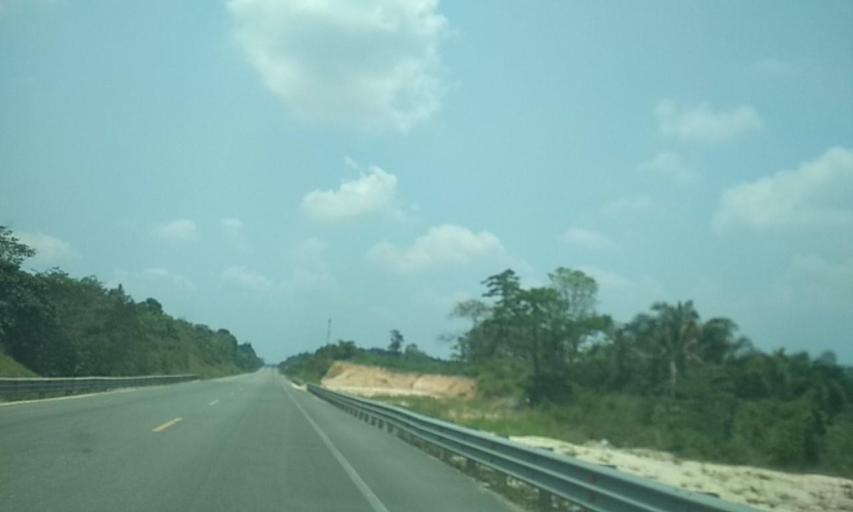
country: MX
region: Tabasco
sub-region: Huimanguillo
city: Francisco Rueda
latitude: 17.7440
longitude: -93.9861
